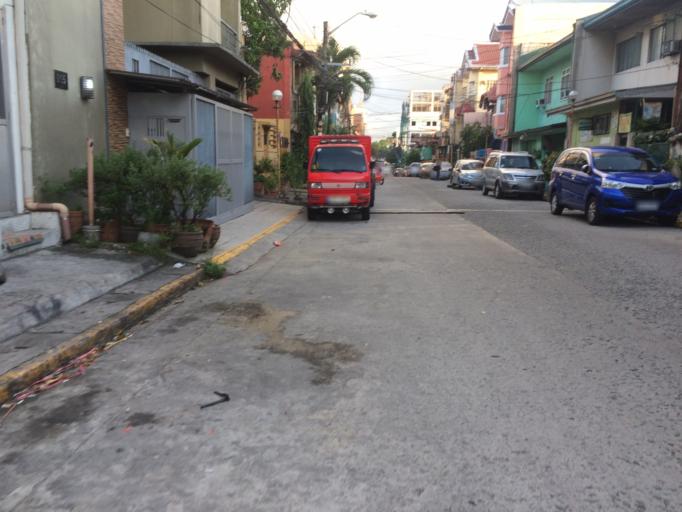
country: PH
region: Metro Manila
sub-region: San Juan
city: San Juan
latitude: 14.6103
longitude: 121.0087
